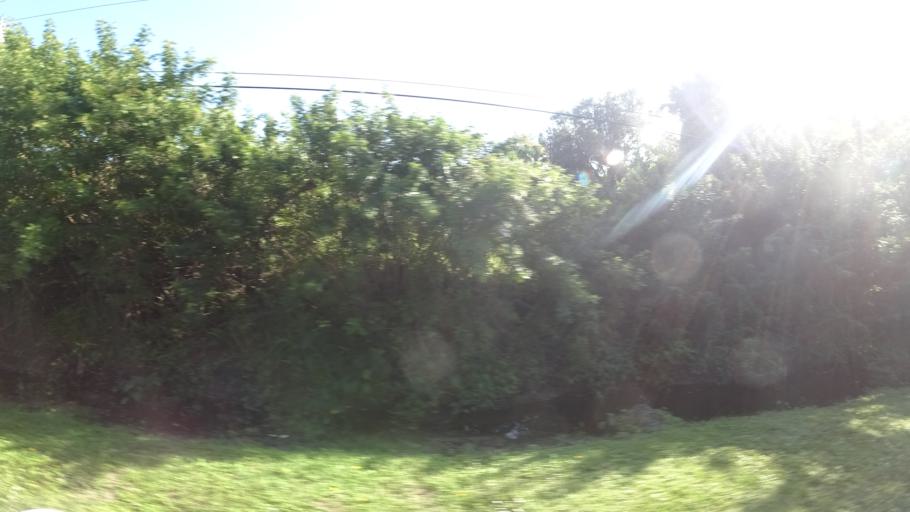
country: US
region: Florida
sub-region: Sarasota County
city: North Sarasota
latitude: 27.3817
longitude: -82.5232
